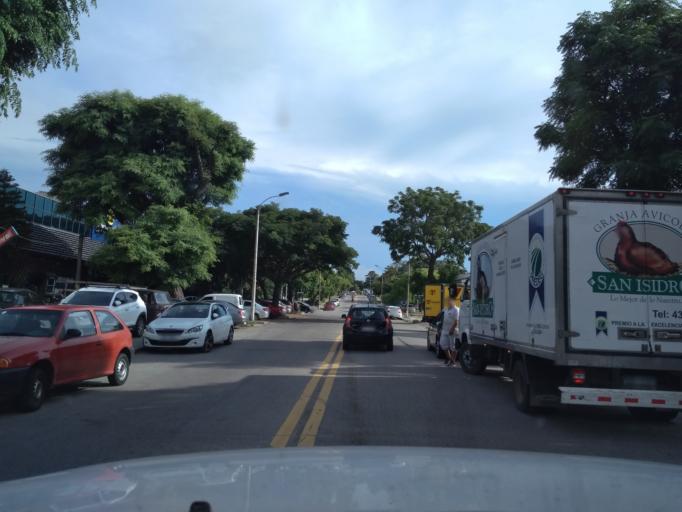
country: UY
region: Canelones
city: Paso de Carrasco
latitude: -34.8931
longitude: -56.0800
